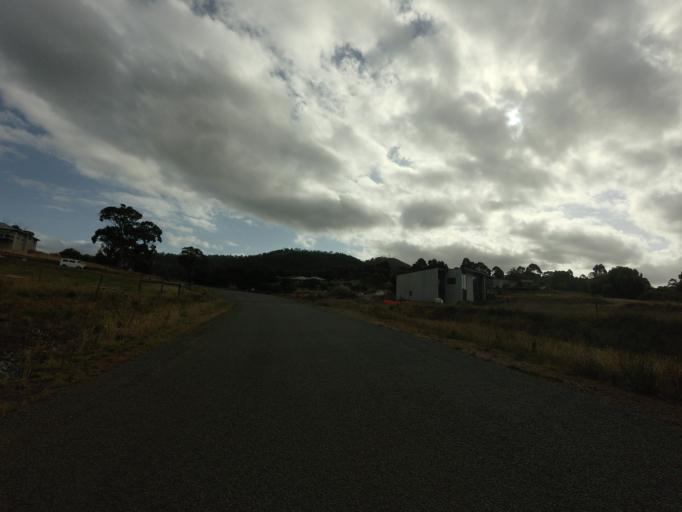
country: AU
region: Tasmania
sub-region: Clarence
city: Acton Park
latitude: -42.8571
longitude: 147.4769
